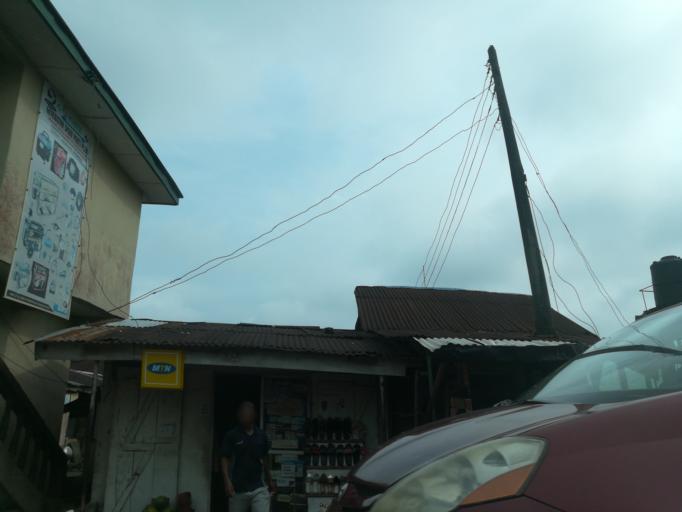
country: NG
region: Rivers
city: Port Harcourt
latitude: 4.8753
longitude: 6.9875
